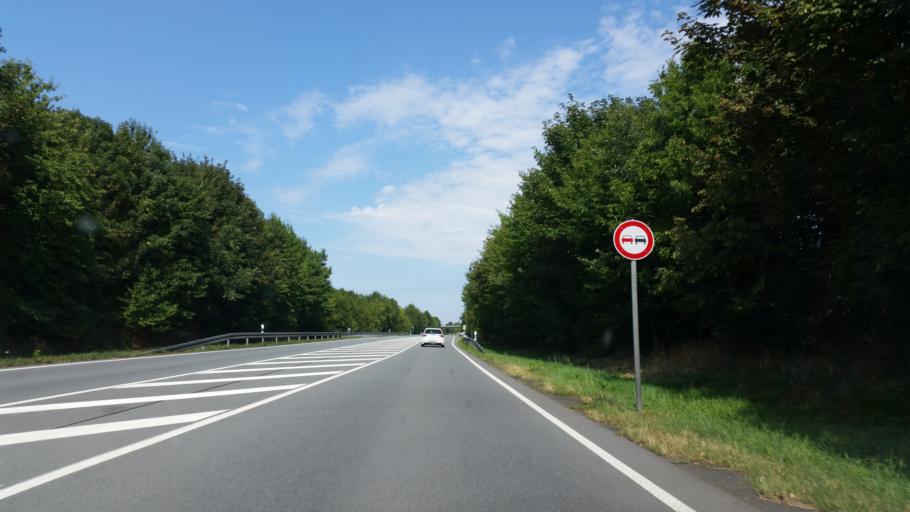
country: DE
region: Saxony
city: Zittau
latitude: 50.9203
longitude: 14.8187
